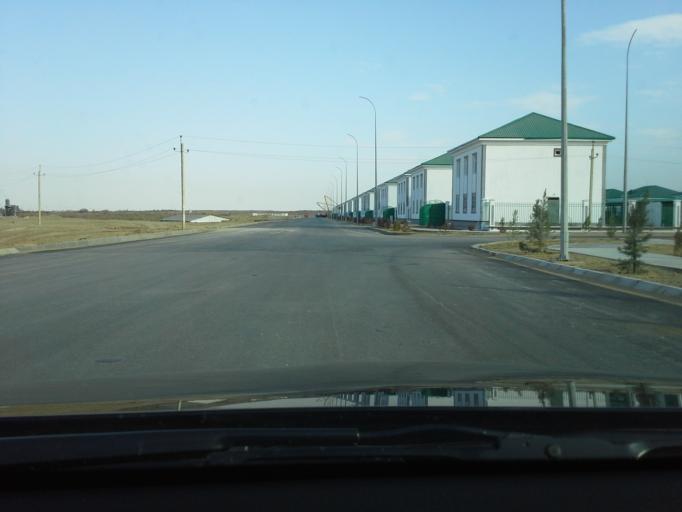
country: TM
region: Ahal
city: Abadan
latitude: 38.1003
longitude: 58.3117
